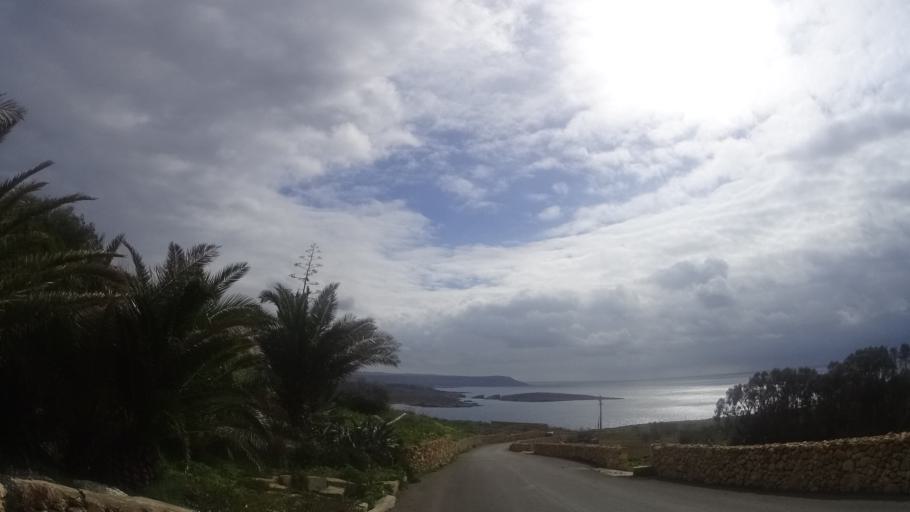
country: MT
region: Il-Qala
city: Qala
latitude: 36.0324
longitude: 14.3215
